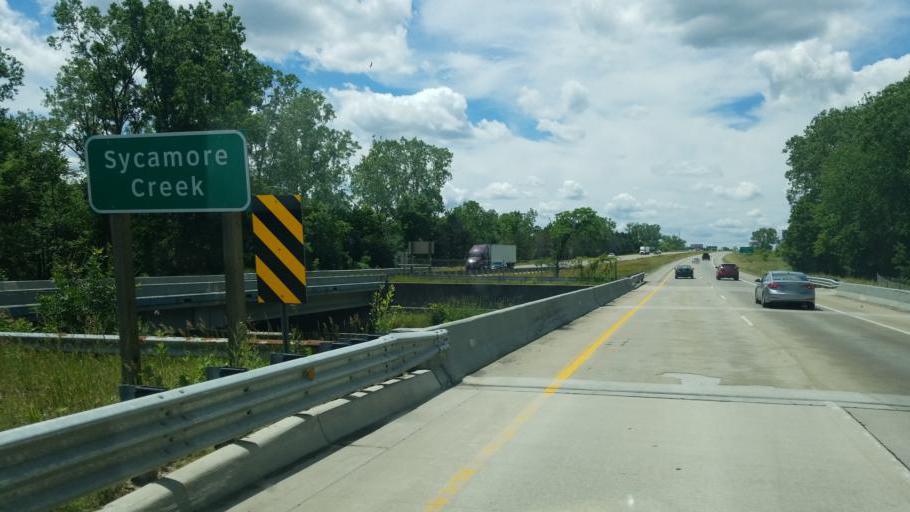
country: US
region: Michigan
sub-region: Ingham County
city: Holt
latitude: 42.6685
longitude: -84.5112
